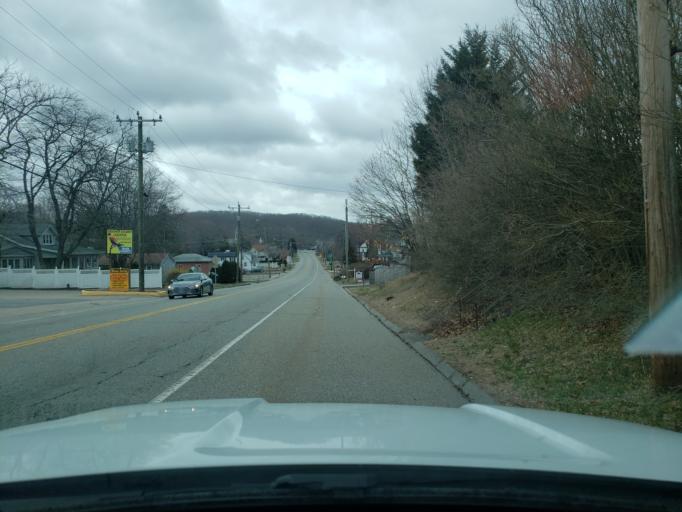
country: US
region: Connecticut
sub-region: New London County
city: Uncasville
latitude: 41.4307
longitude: -72.1102
